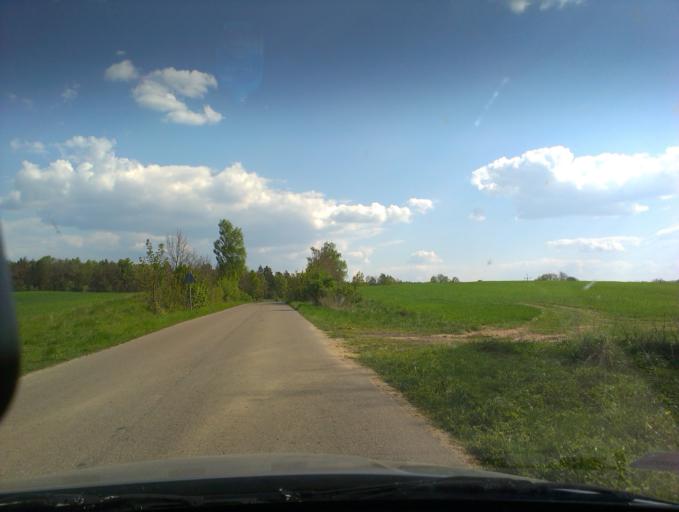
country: PL
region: West Pomeranian Voivodeship
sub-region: Powiat szczecinecki
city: Barwice
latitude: 53.7162
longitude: 16.3009
